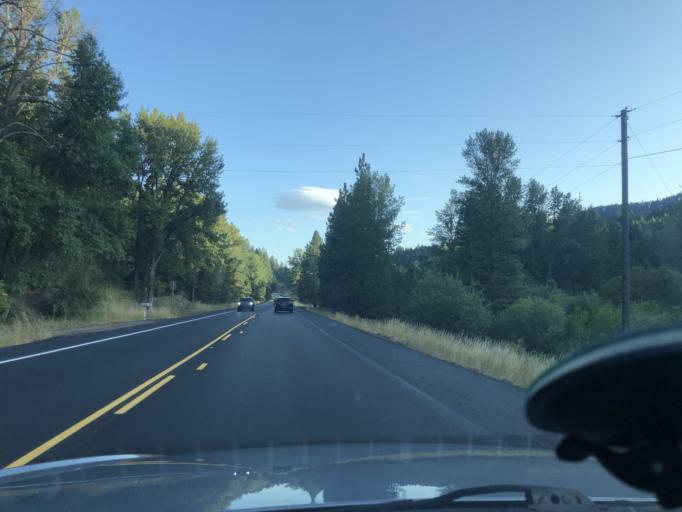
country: US
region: Washington
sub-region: Kittitas County
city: Cle Elum
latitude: 47.2364
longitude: -120.6948
